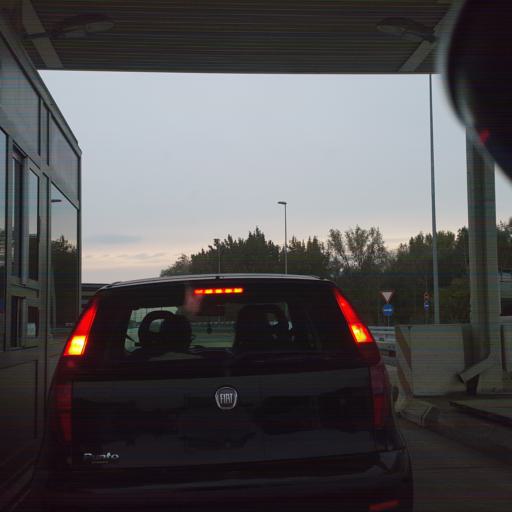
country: RS
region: Autonomna Pokrajina Vojvodina
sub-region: Juznobacki Okrug
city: Petrovaradin
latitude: 45.2883
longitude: 19.8911
